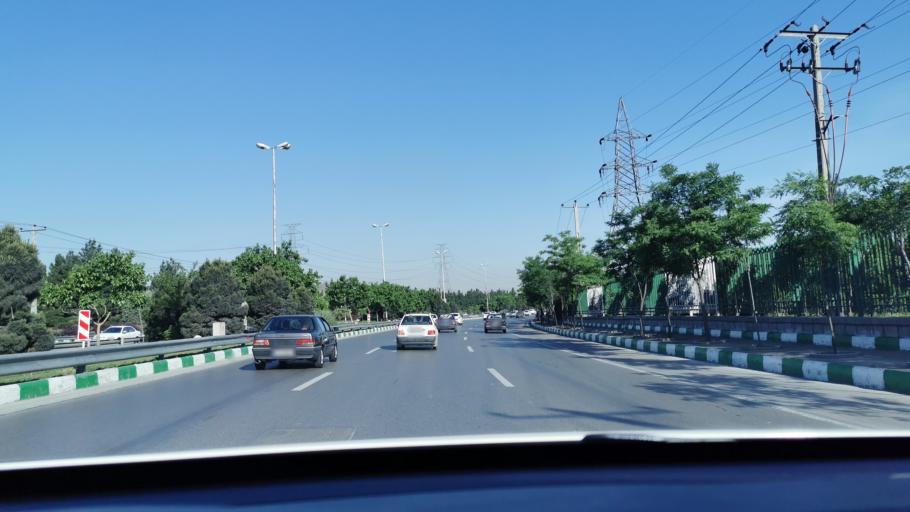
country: IR
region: Razavi Khorasan
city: Mashhad
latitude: 36.2575
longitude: 59.5901
